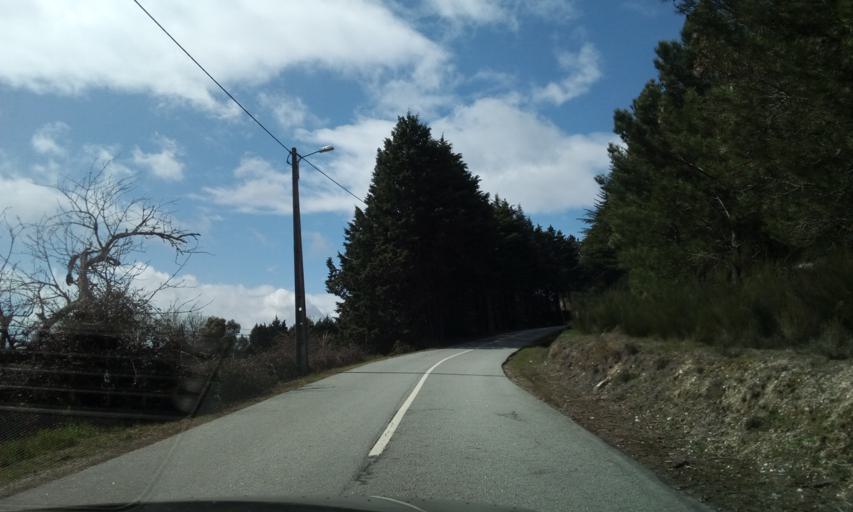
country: PT
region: Guarda
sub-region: Fornos de Algodres
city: Fornos de Algodres
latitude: 40.6317
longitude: -7.5435
